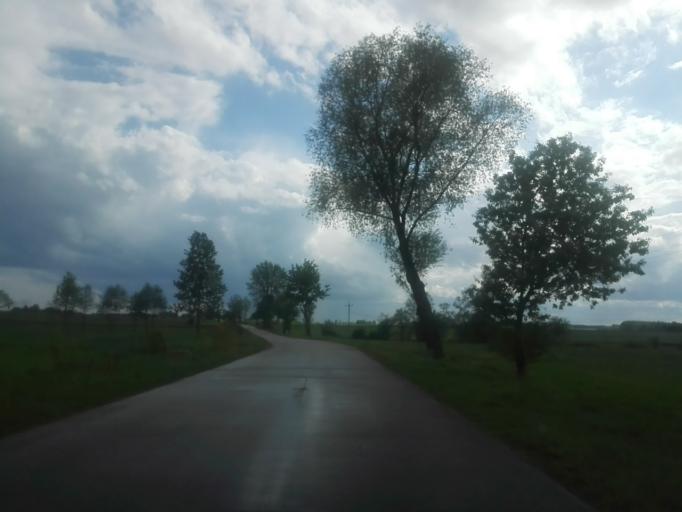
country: PL
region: Podlasie
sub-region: Powiat lomzynski
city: Wizna
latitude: 53.2528
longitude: 22.4392
